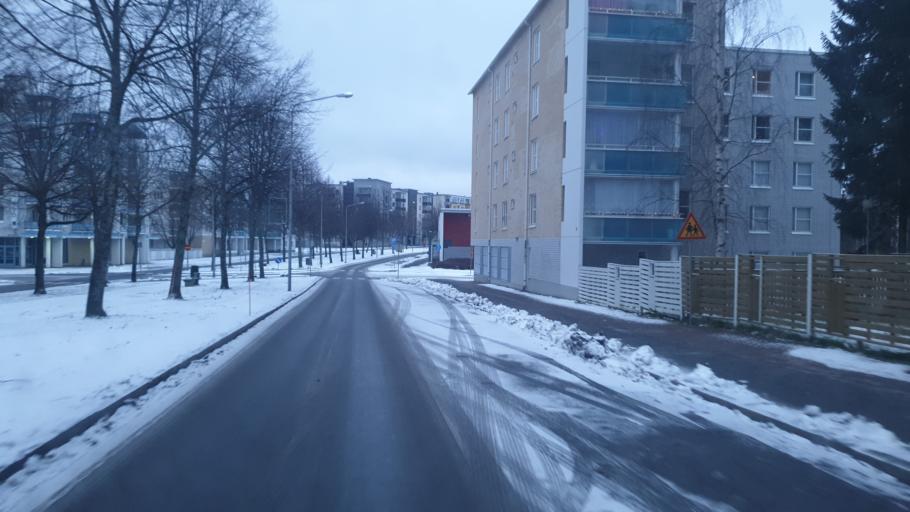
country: FI
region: Northern Savo
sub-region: Kuopio
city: Kuopio
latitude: 62.8388
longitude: 27.6405
